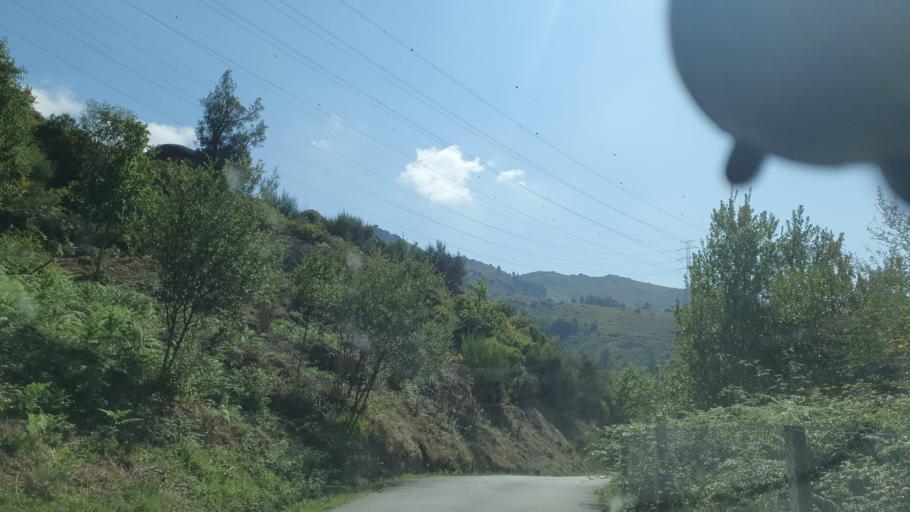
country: PT
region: Braga
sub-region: Vieira do Minho
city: Vieira do Minho
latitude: 41.6734
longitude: -8.1311
